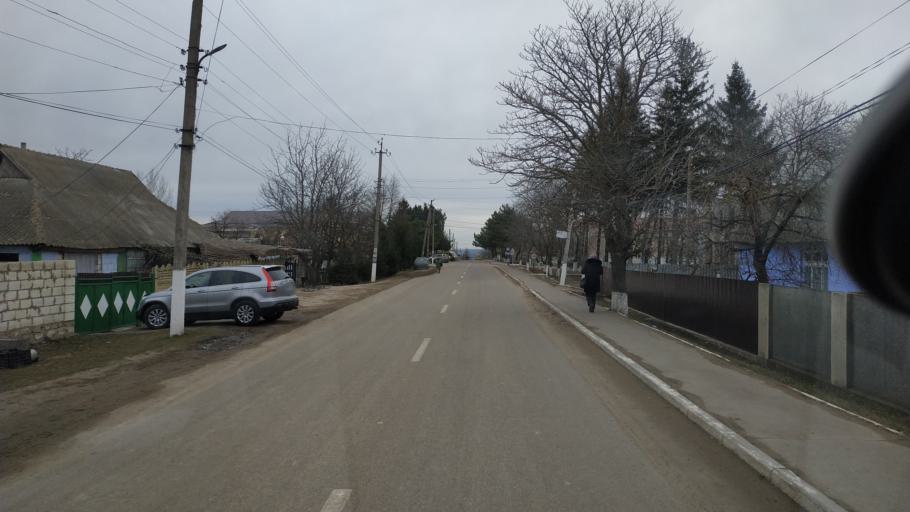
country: MD
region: Telenesti
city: Cocieri
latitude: 47.3118
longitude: 29.0652
